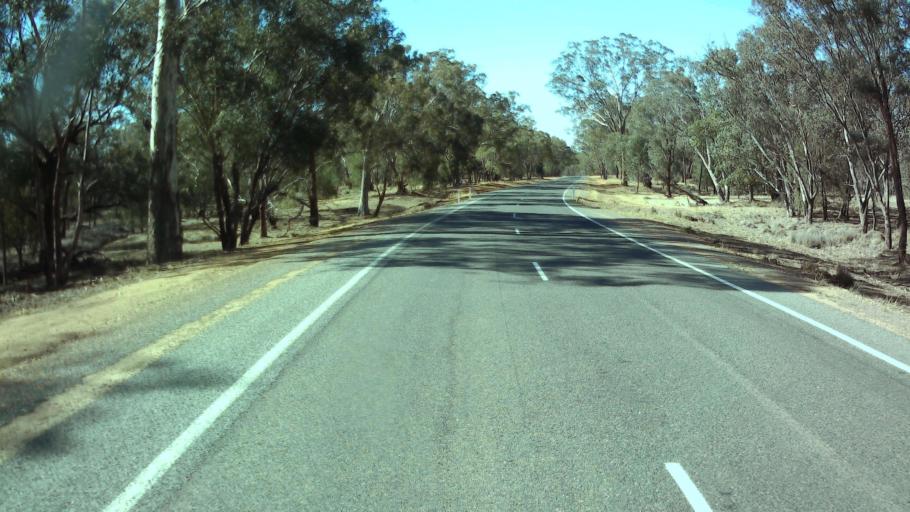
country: AU
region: New South Wales
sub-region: Weddin
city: Grenfell
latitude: -33.7635
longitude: 148.0818
